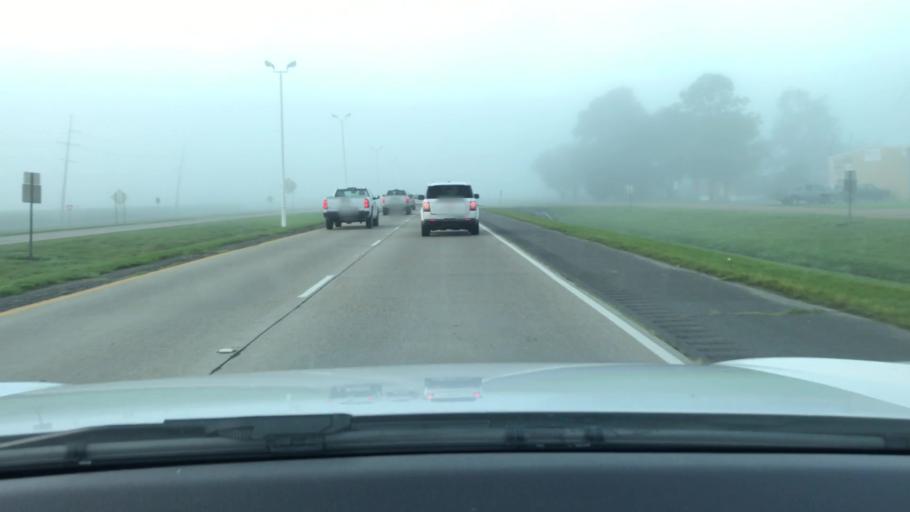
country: US
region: Louisiana
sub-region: West Baton Rouge Parish
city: Addis
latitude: 30.3542
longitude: -91.2591
